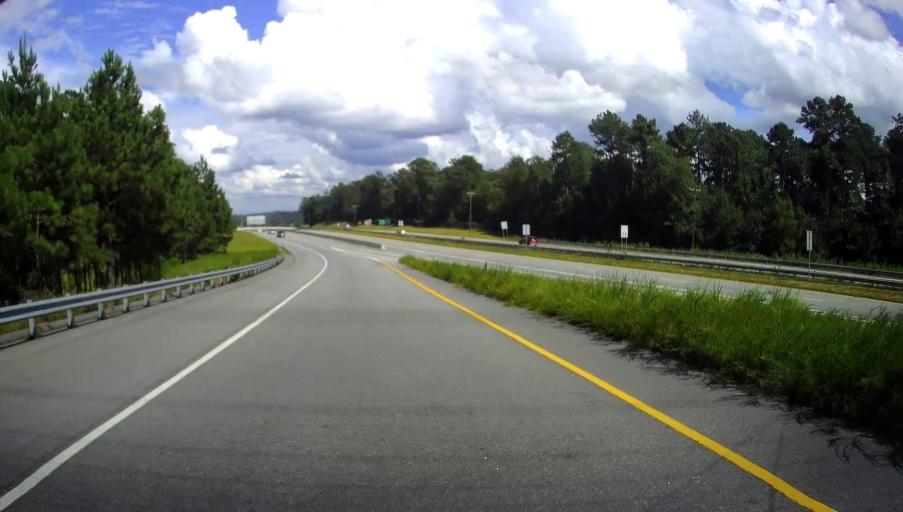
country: US
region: Georgia
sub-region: Muscogee County
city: Columbus
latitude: 32.4055
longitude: -84.9202
